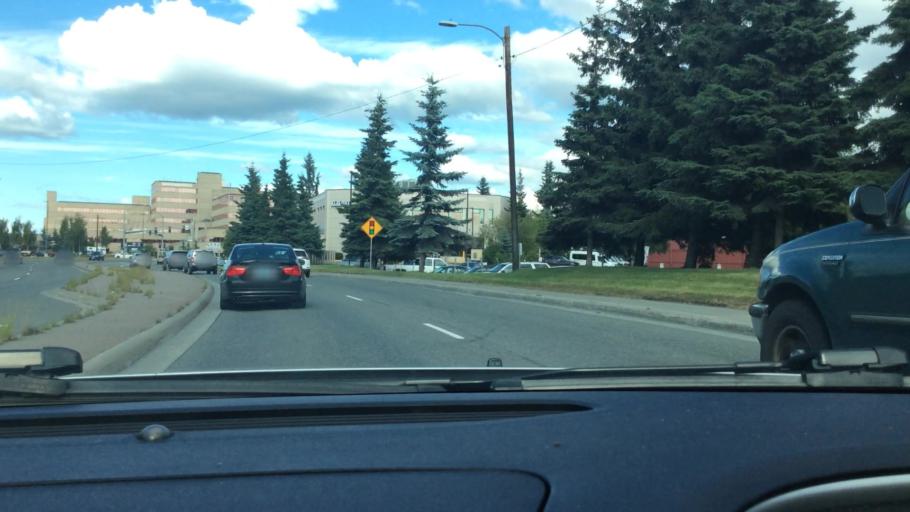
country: US
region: Alaska
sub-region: Anchorage Municipality
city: Anchorage
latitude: 61.2081
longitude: -149.8342
